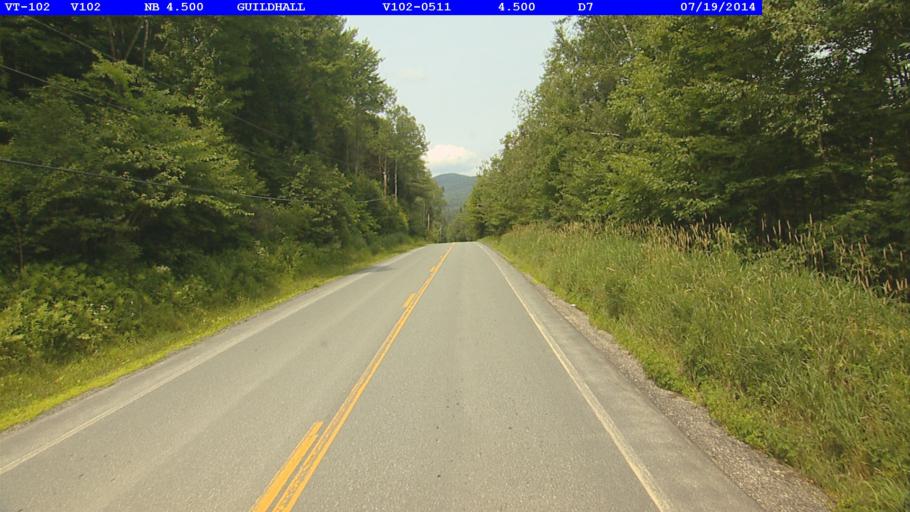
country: US
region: Vermont
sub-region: Essex County
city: Guildhall
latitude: 44.5526
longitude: -71.5964
